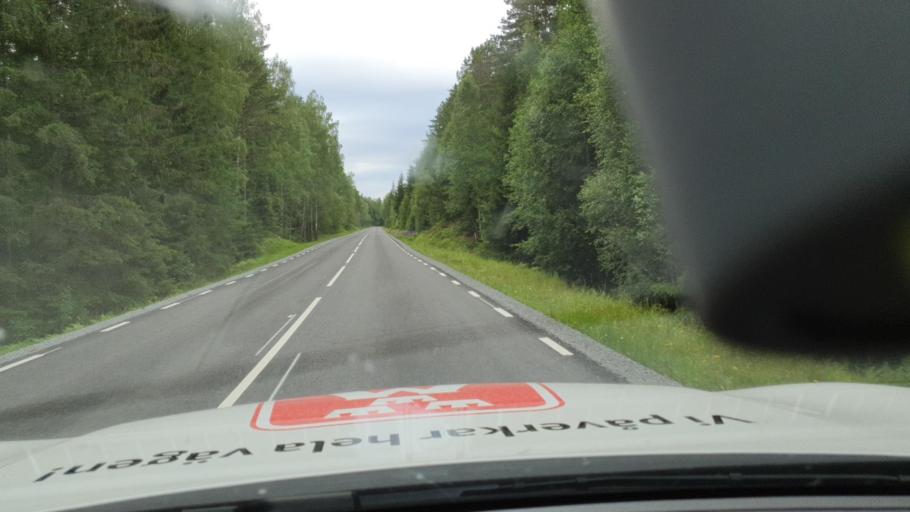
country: SE
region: OErebro
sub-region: Laxa Kommun
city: Laxa
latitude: 58.8736
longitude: 14.5216
